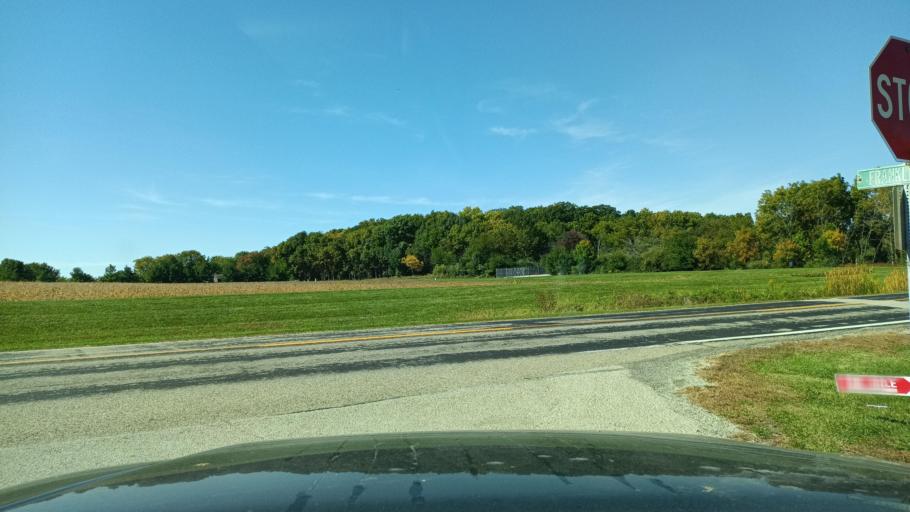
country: US
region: Illinois
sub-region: Champaign County
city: Lake of the Woods
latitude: 40.2068
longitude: -88.3652
